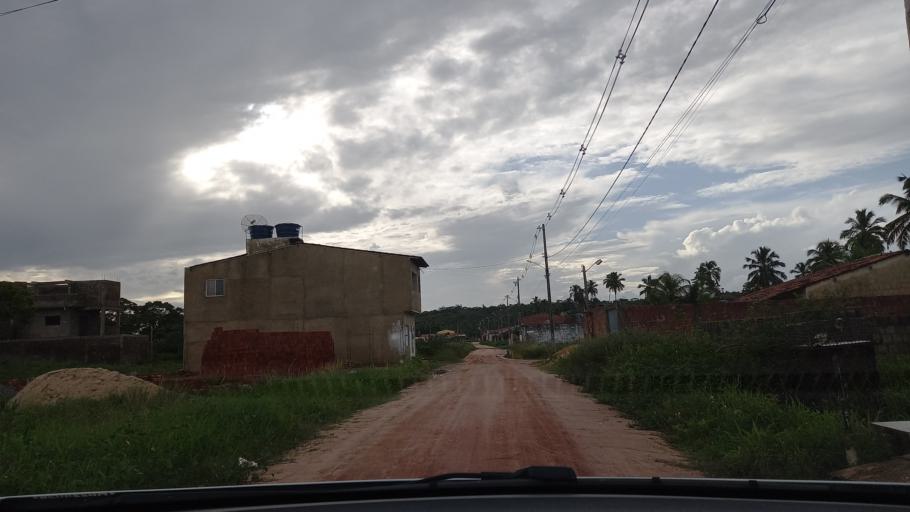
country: BR
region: Pernambuco
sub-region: Sao Jose Da Coroa Grande
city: Sao Jose da Coroa Grande
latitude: -8.9212
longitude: -35.1630
